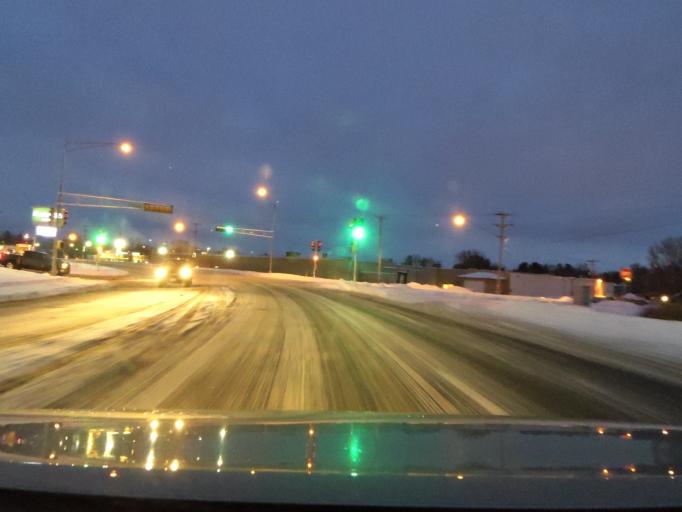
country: US
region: Wisconsin
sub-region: Dunn County
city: Menomonie
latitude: 44.9014
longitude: -91.9354
